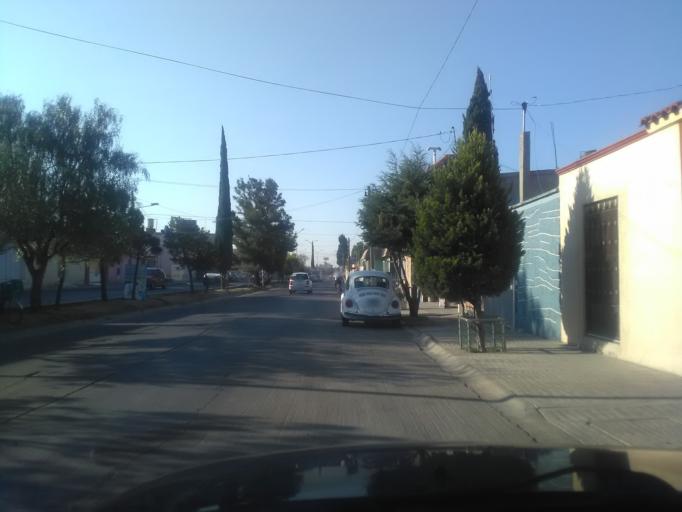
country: MX
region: Durango
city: Victoria de Durango
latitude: 24.0427
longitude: -104.6216
